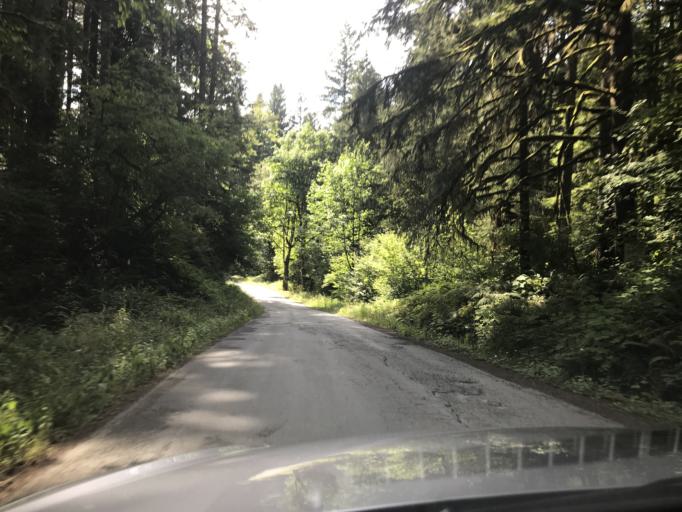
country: US
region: Washington
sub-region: King County
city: Hobart
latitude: 47.4165
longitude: -121.9181
